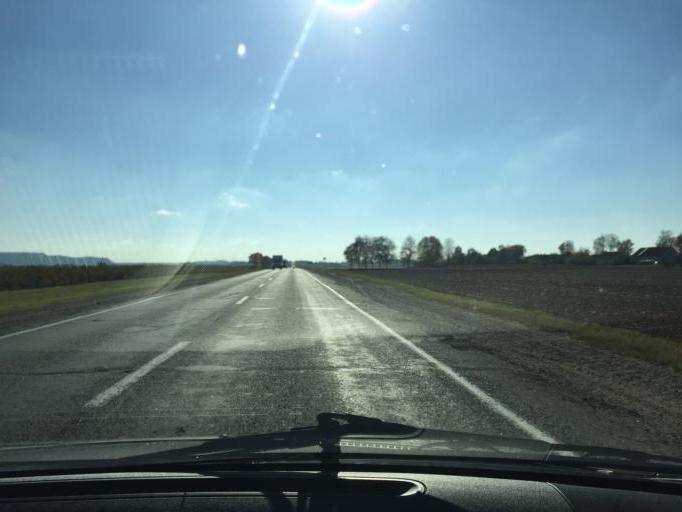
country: BY
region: Minsk
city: Slutsk
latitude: 52.9386
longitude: 27.4898
